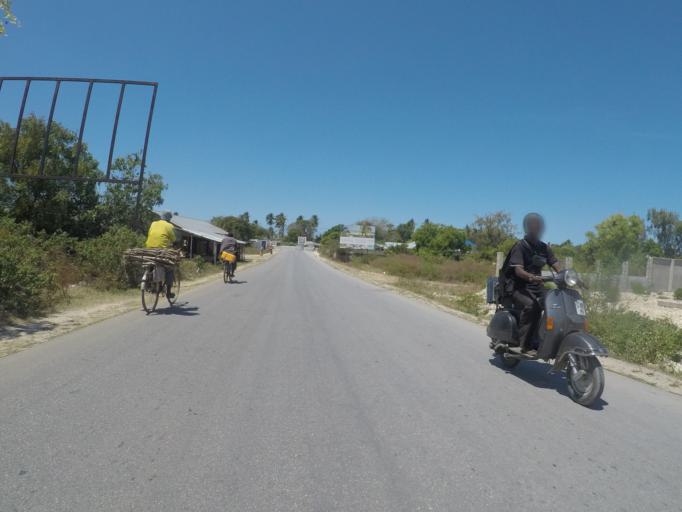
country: TZ
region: Zanzibar Central/South
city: Nganane
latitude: -6.2667
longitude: 39.5298
